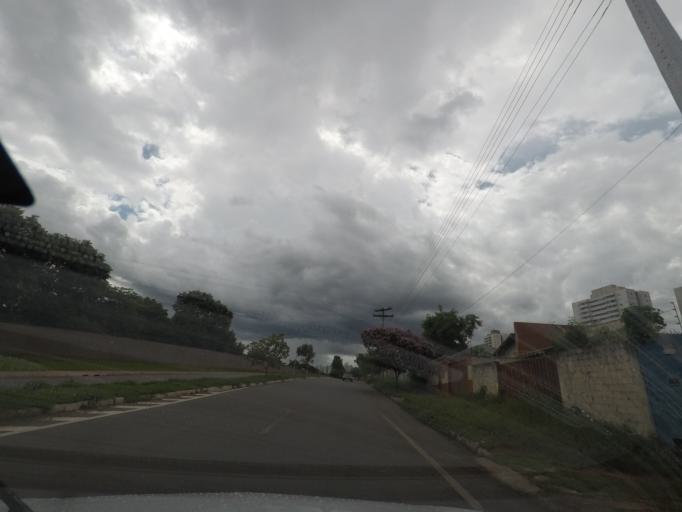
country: BR
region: Goias
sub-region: Goiania
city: Goiania
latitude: -16.7154
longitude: -49.3224
